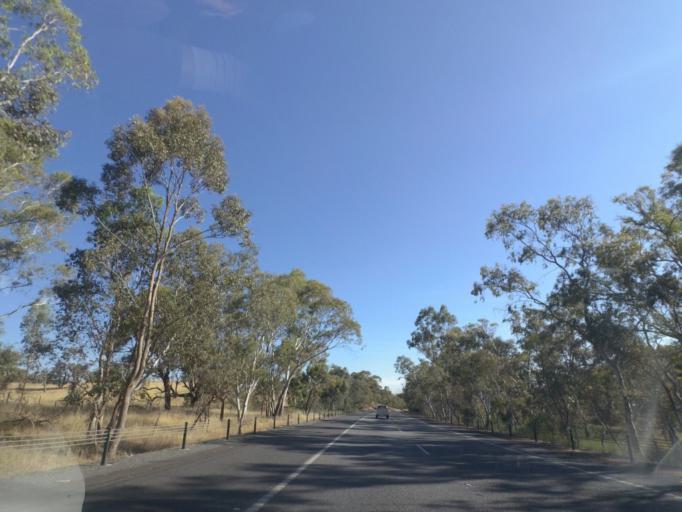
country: AU
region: Victoria
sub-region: Murrindindi
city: Kinglake West
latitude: -37.1673
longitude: 145.0777
